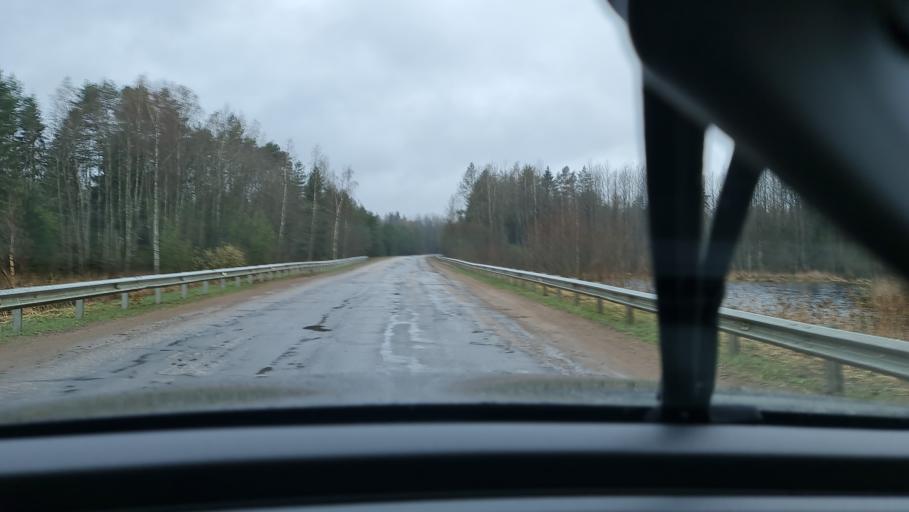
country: RU
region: Novgorod
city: Valday
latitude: 58.0383
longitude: 32.8996
